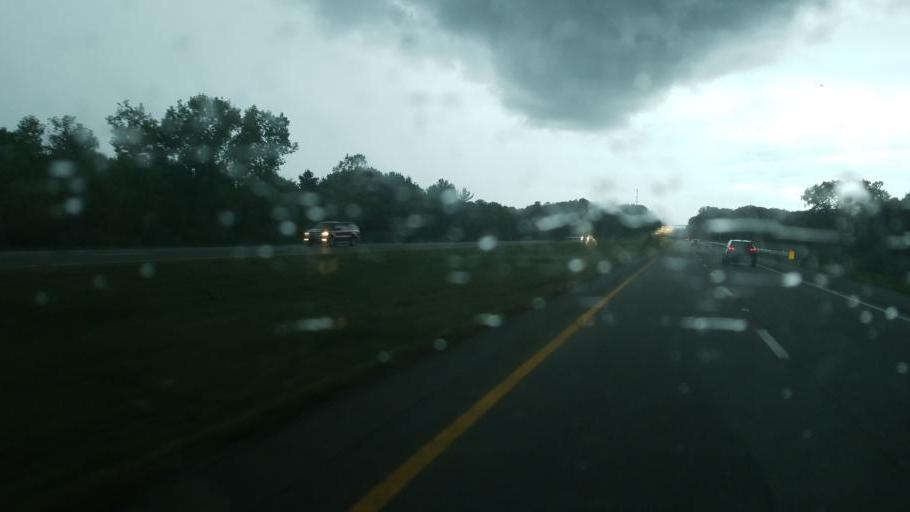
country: US
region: Ohio
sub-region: Geauga County
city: Bainbridge
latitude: 41.3834
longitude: -81.3043
